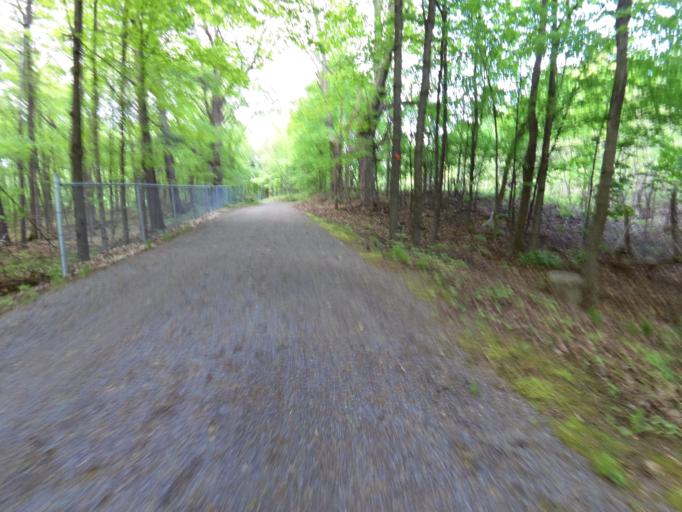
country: CA
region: Ontario
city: Bells Corners
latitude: 45.3393
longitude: -75.8700
